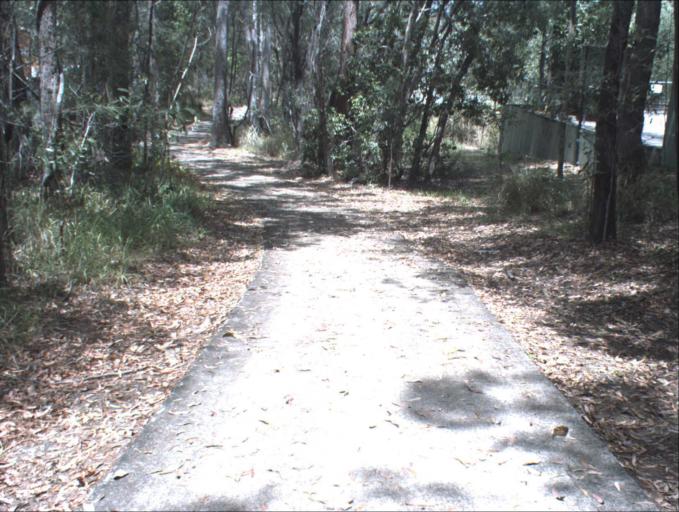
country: AU
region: Queensland
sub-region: Logan
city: Slacks Creek
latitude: -27.6527
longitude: 153.1685
